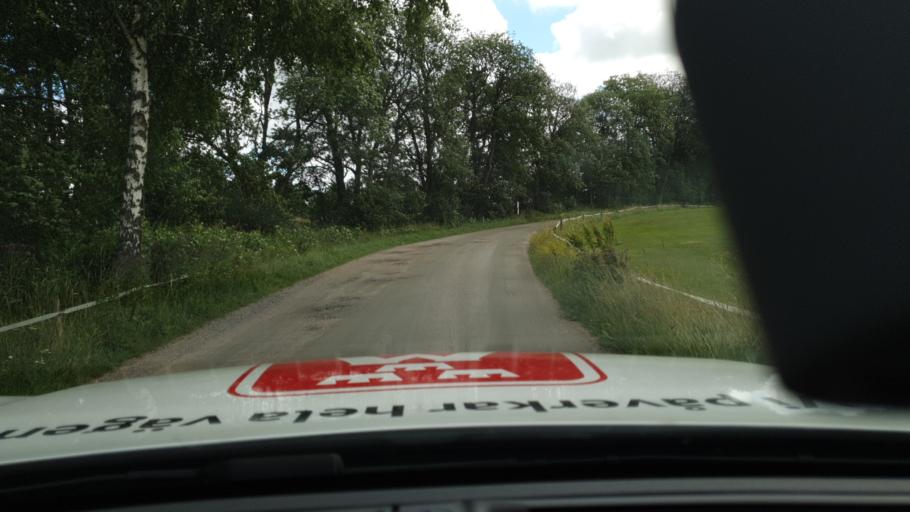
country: SE
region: Vaestra Goetaland
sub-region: Falkopings Kommun
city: Falkoeping
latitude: 58.1378
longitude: 13.6008
